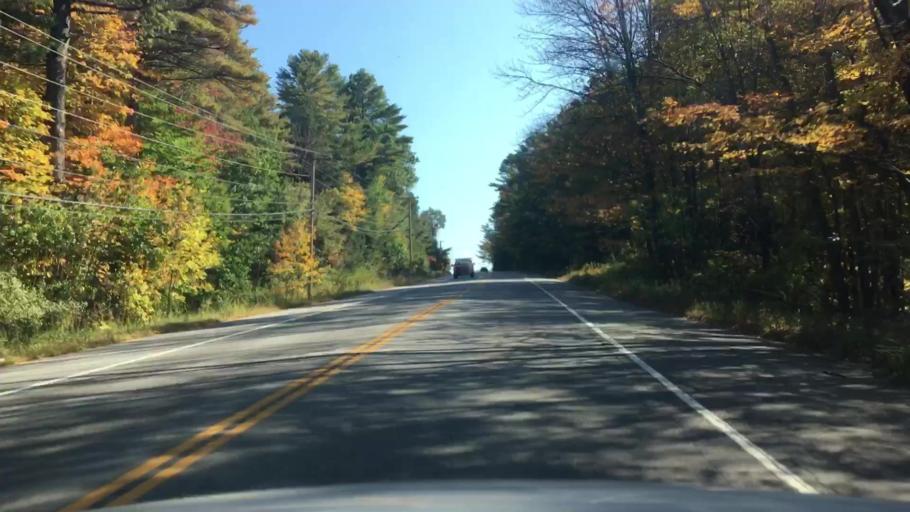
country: US
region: Maine
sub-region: Androscoggin County
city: Lisbon Falls
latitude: 43.9821
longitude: -70.0334
